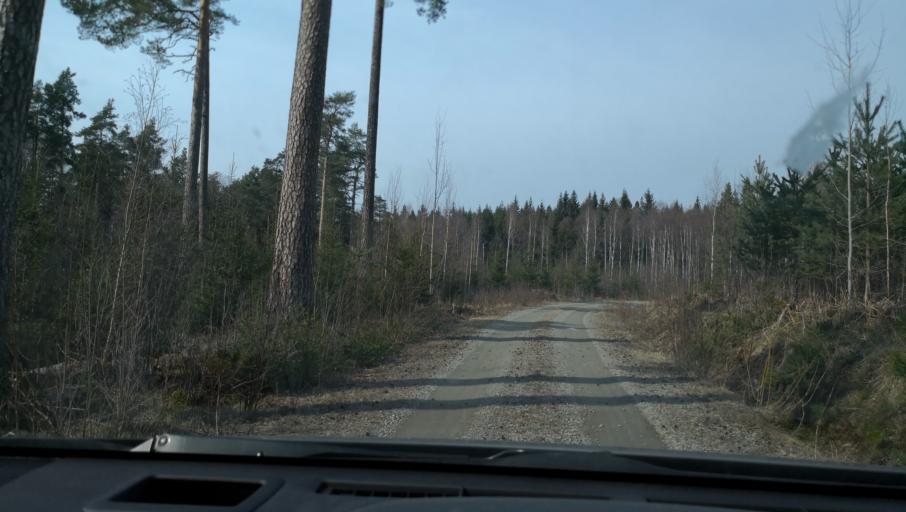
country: SE
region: OErebro
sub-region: Lindesbergs Kommun
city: Frovi
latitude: 59.3740
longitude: 15.4245
